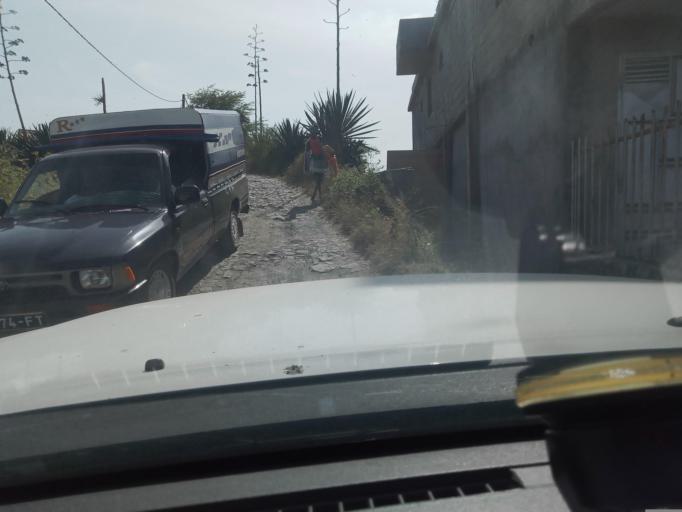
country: CV
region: Santa Catarina
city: Assomada
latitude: 15.1335
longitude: -23.6642
